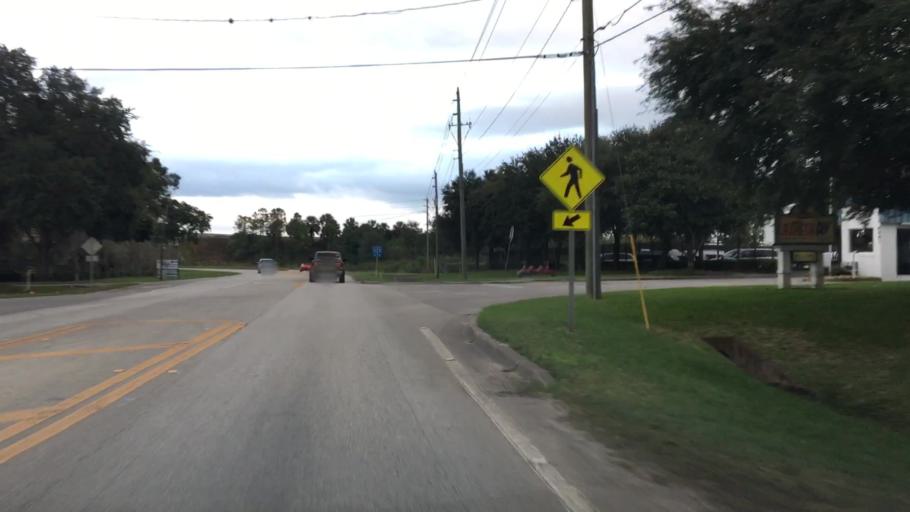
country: US
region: Florida
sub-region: Volusia County
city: DeBary
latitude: 28.8296
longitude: -81.3281
